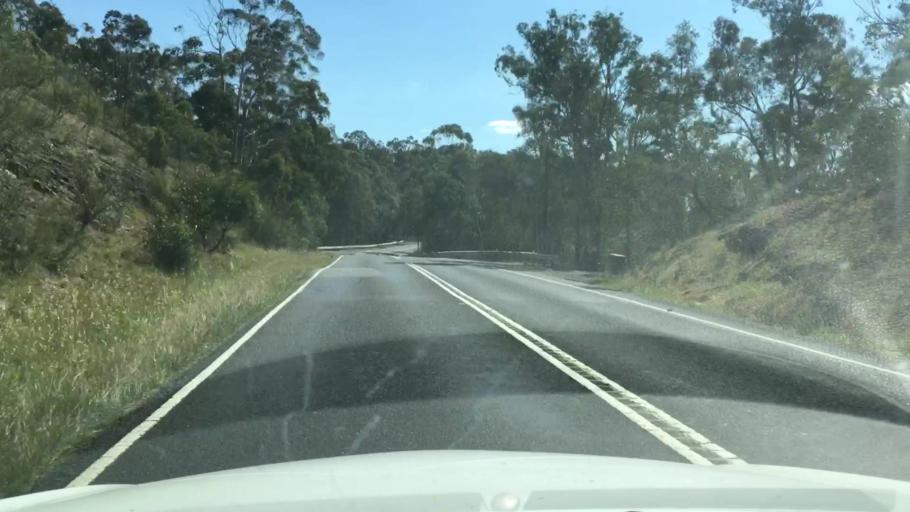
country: AU
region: Victoria
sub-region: Nillumbik
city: Saint Andrews
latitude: -37.6639
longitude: 145.2683
